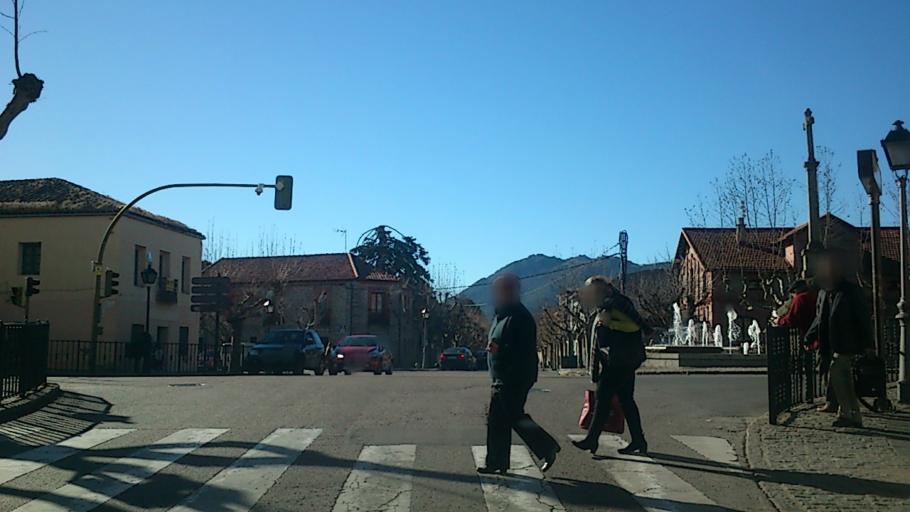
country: ES
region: Madrid
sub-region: Provincia de Madrid
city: El Escorial
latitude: 40.5834
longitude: -4.1305
